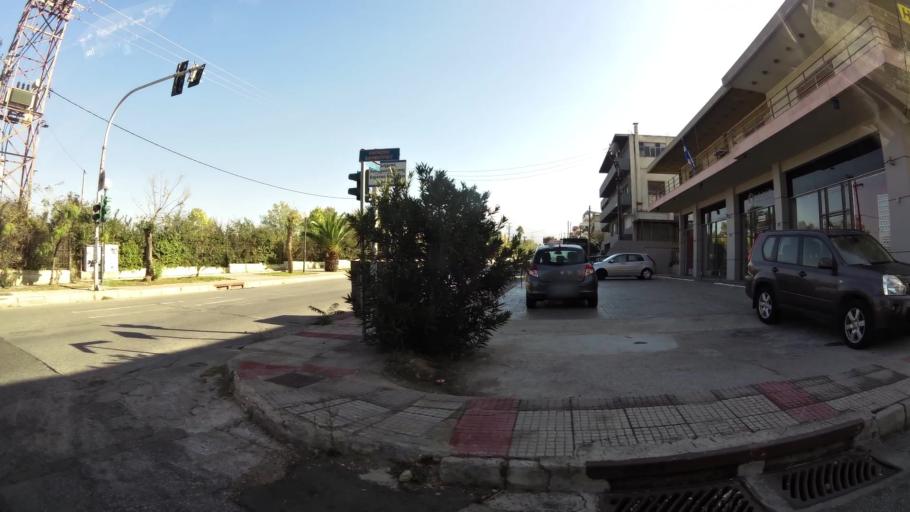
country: GR
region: Attica
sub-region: Nomarchia Athinas
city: Lykovrysi
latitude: 38.0687
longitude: 23.7745
